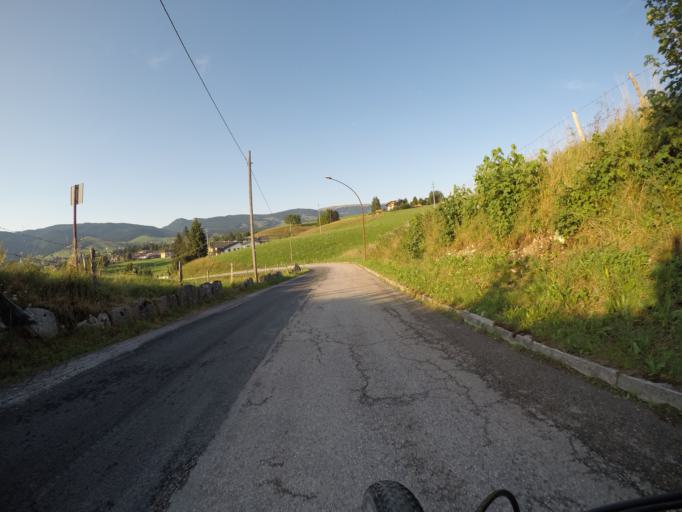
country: IT
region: Veneto
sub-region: Provincia di Vicenza
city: Asiago
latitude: 45.8651
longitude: 11.5108
